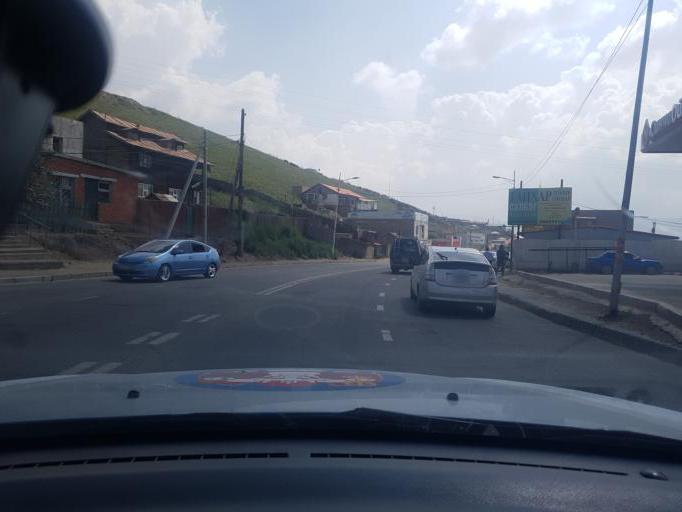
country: MN
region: Ulaanbaatar
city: Ulaanbaatar
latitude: 47.9406
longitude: 106.8823
